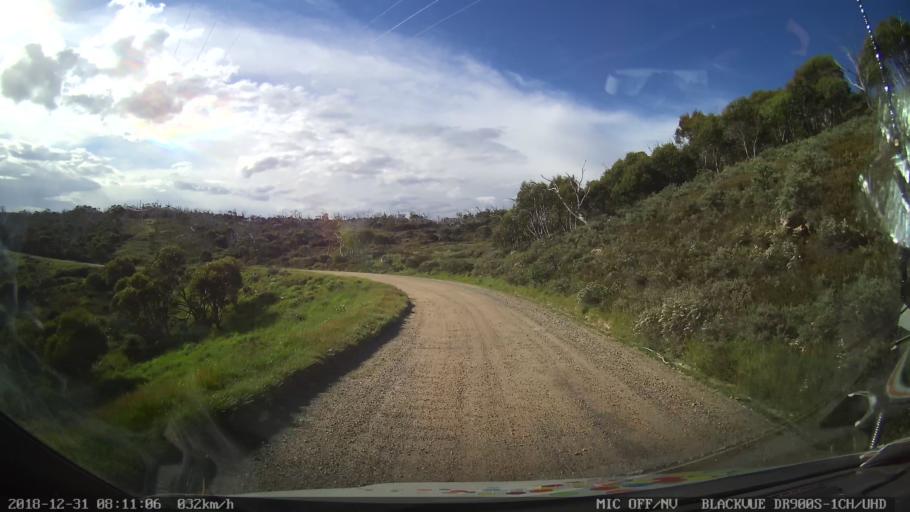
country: AU
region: New South Wales
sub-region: Snowy River
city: Jindabyne
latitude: -36.3851
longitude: 148.4244
